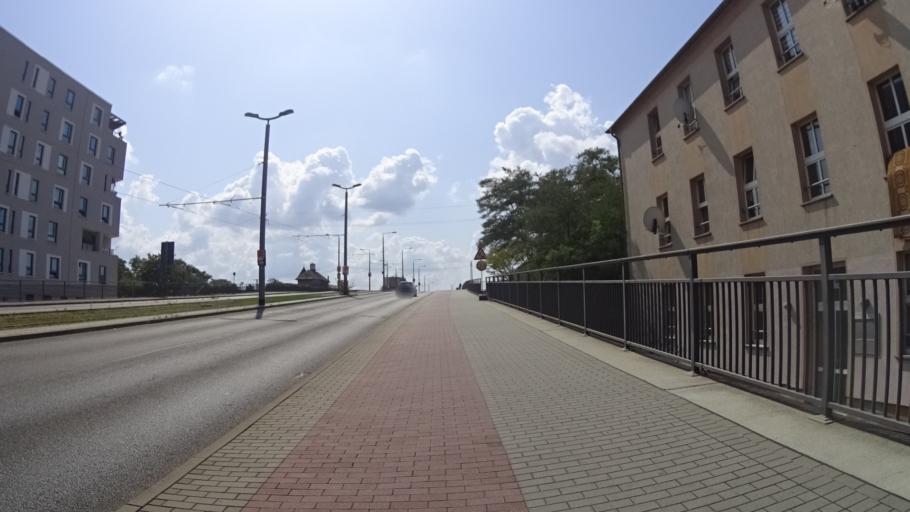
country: DE
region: Brandenburg
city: Cottbus
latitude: 51.7528
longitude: 14.3282
